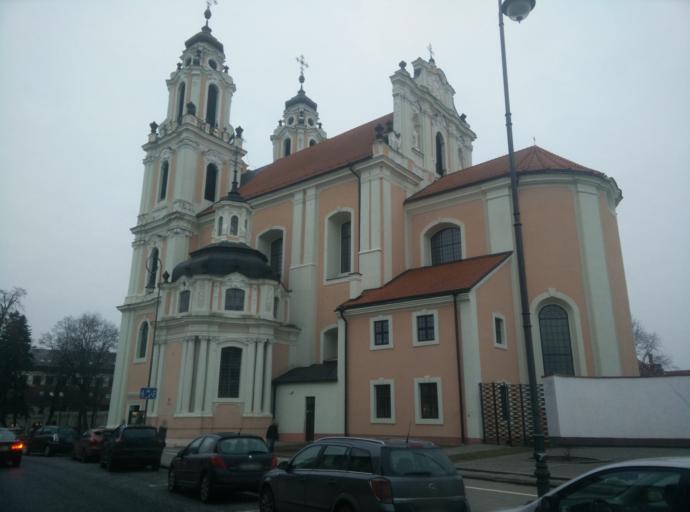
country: LT
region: Vilnius County
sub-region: Vilnius
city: Vilnius
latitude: 54.6814
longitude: 25.2810
